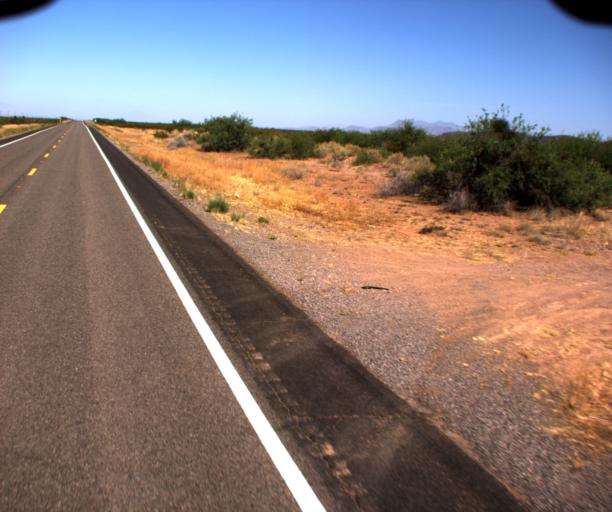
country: US
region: Arizona
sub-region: Graham County
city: Swift Trail Junction
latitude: 32.7566
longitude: -109.4264
